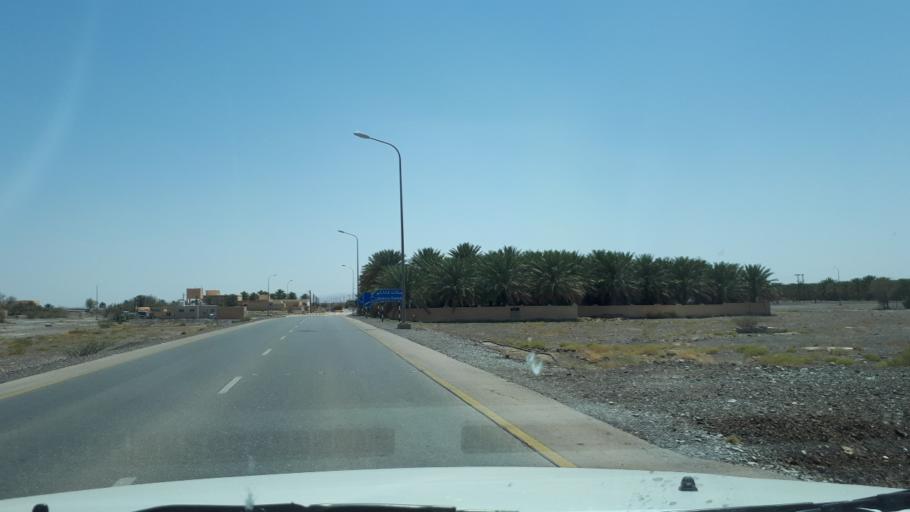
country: OM
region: Muhafazat ad Dakhiliyah
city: Bahla'
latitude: 22.9156
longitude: 57.2529
